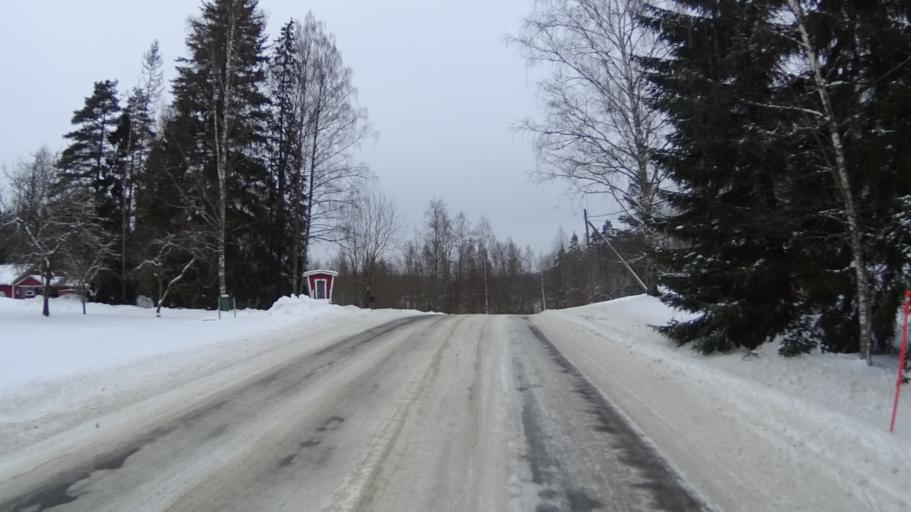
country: FI
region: Uusimaa
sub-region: Helsinki
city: Karkkila
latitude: 60.5014
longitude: 24.1396
